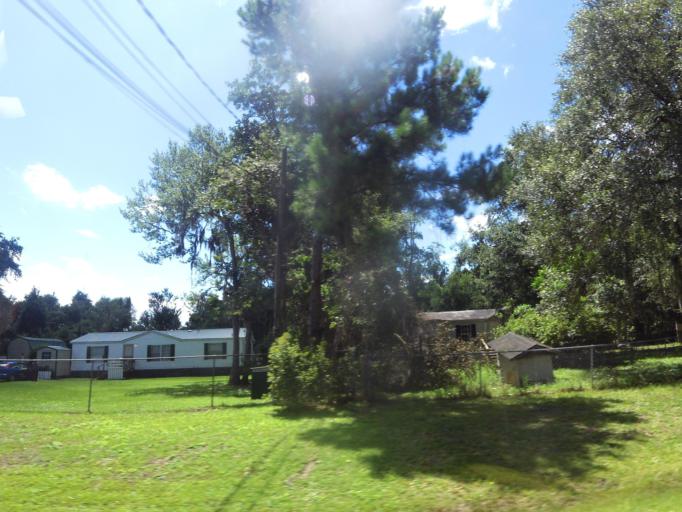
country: US
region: Georgia
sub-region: Camden County
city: St. Marys
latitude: 30.6677
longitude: -81.5341
